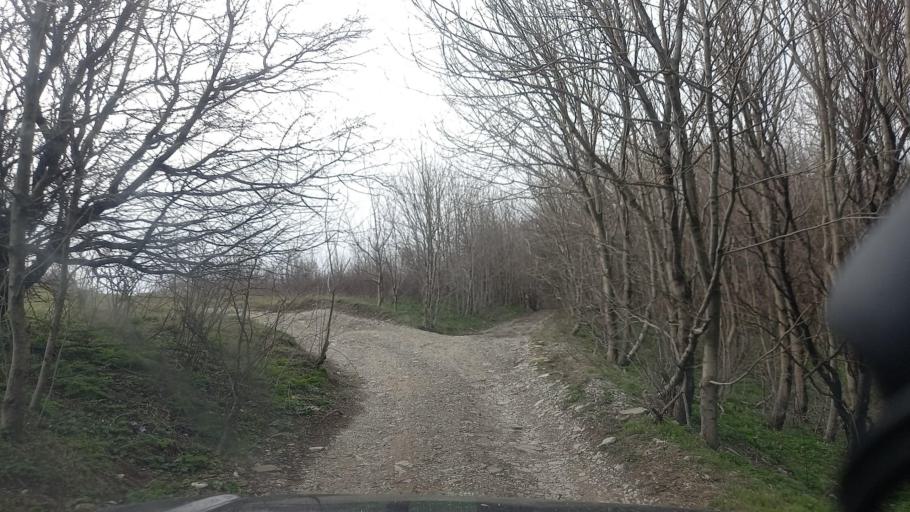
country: RU
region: Krasnodarskiy
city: Divnomorskoye
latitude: 44.6137
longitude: 38.2237
